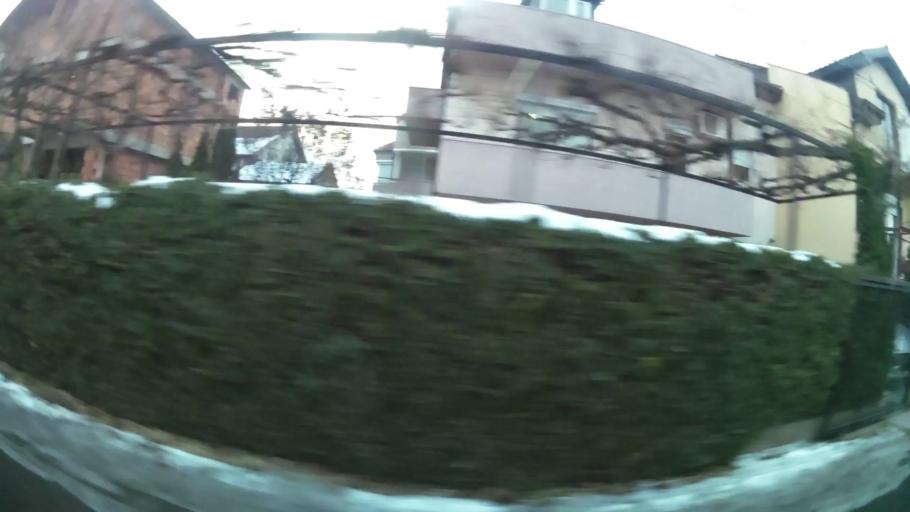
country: MK
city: Creshevo
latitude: 42.0116
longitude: 21.5167
